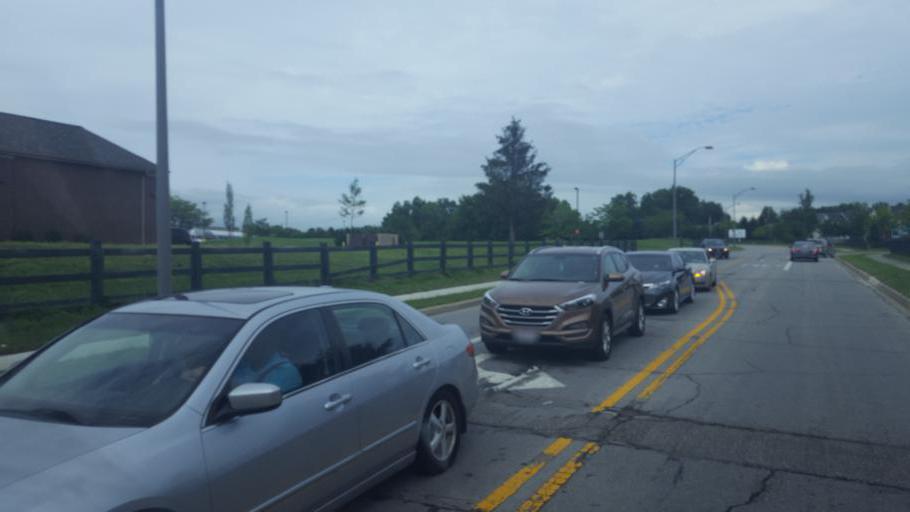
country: US
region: Ohio
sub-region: Franklin County
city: Gahanna
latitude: 40.0581
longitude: -82.8627
